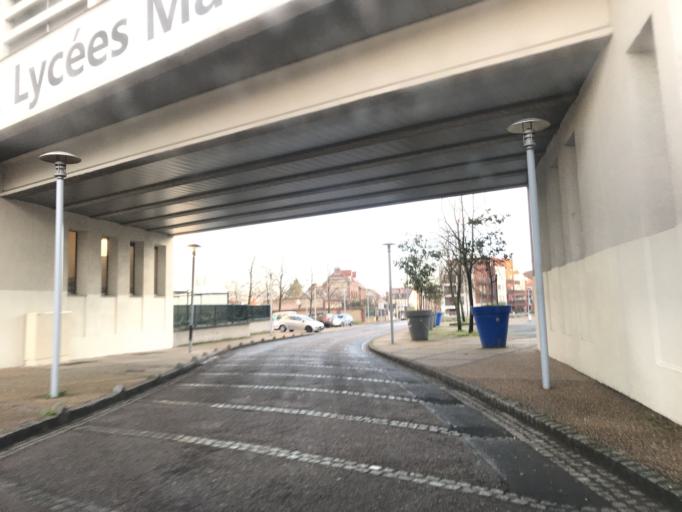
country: FR
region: Haute-Normandie
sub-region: Departement de la Seine-Maritime
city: Sotteville-les-Rouen
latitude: 49.4148
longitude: 1.0852
